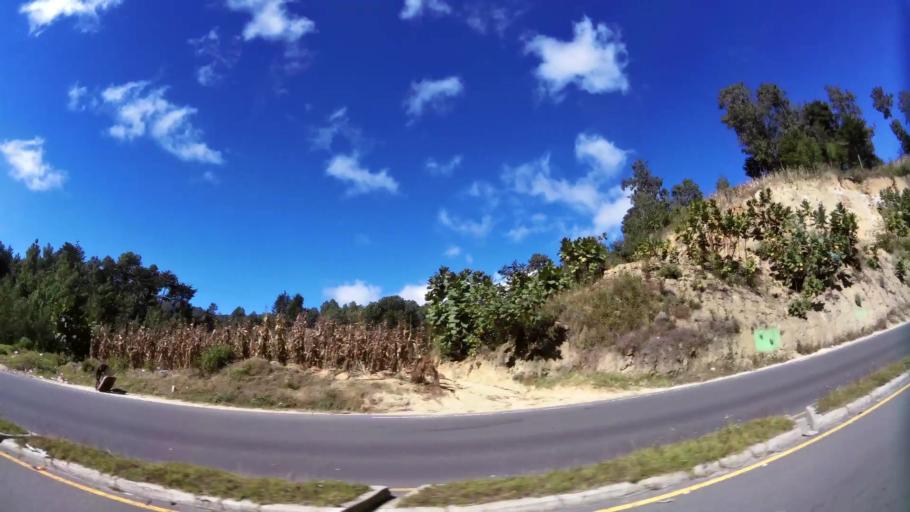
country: GT
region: Solola
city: Nahuala
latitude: 14.8337
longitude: -91.3307
